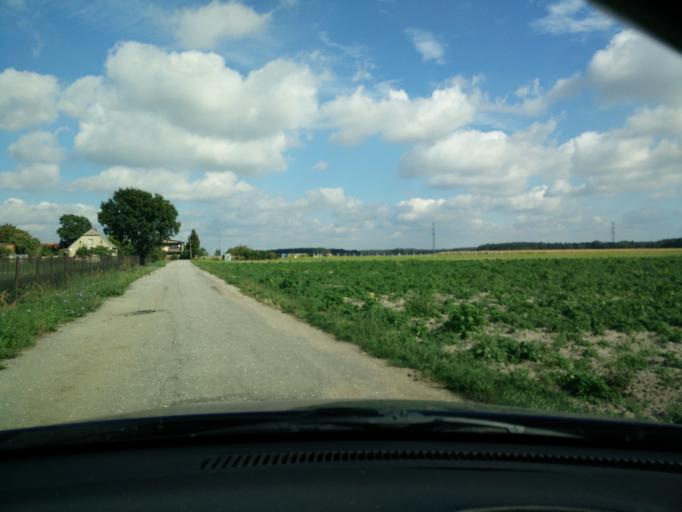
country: PL
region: Greater Poland Voivodeship
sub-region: Powiat sredzki
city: Dominowo
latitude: 52.2872
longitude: 17.3876
